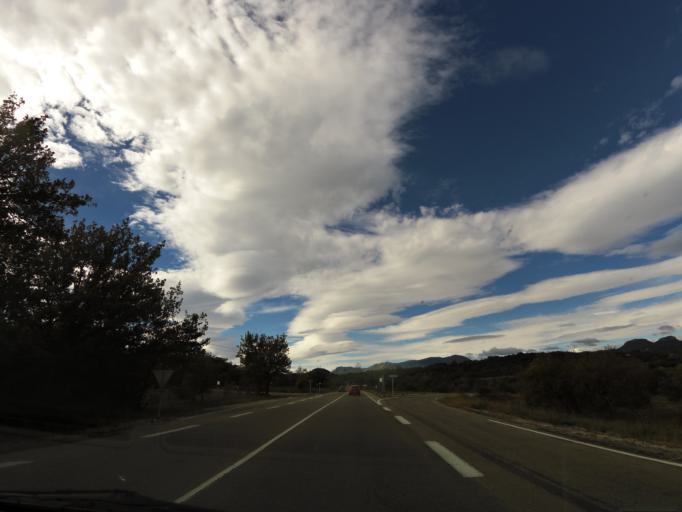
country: FR
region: Languedoc-Roussillon
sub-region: Departement du Gard
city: Sauve
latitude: 43.9470
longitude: 3.9055
